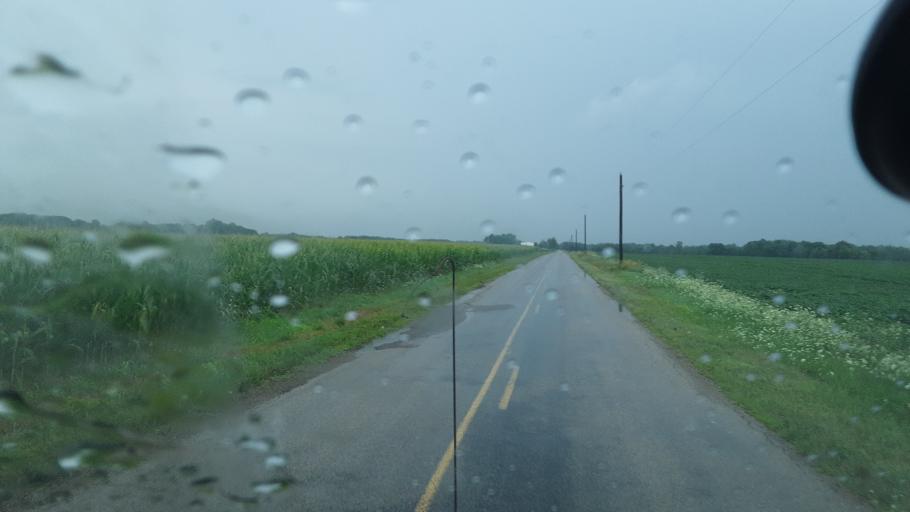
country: US
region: Ohio
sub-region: Williams County
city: Edgerton
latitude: 41.5025
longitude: -84.8150
